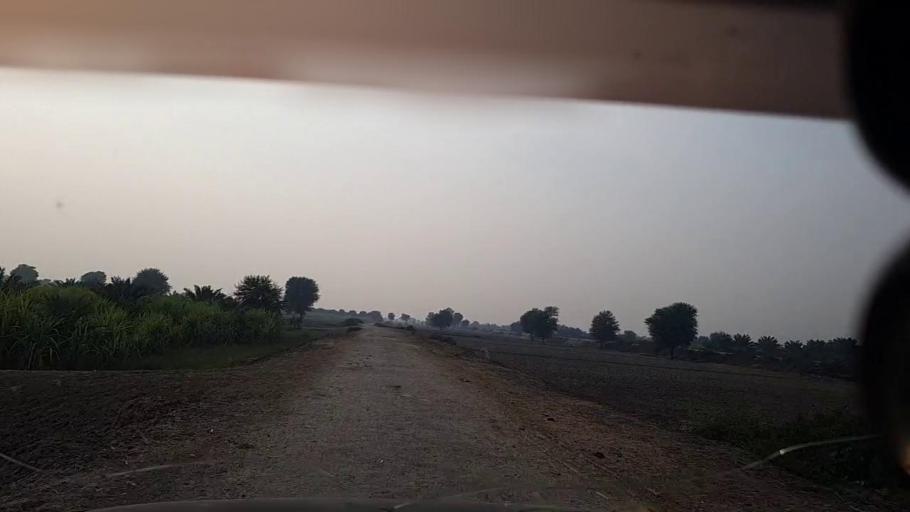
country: PK
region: Sindh
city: Gambat
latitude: 27.4355
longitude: 68.6039
